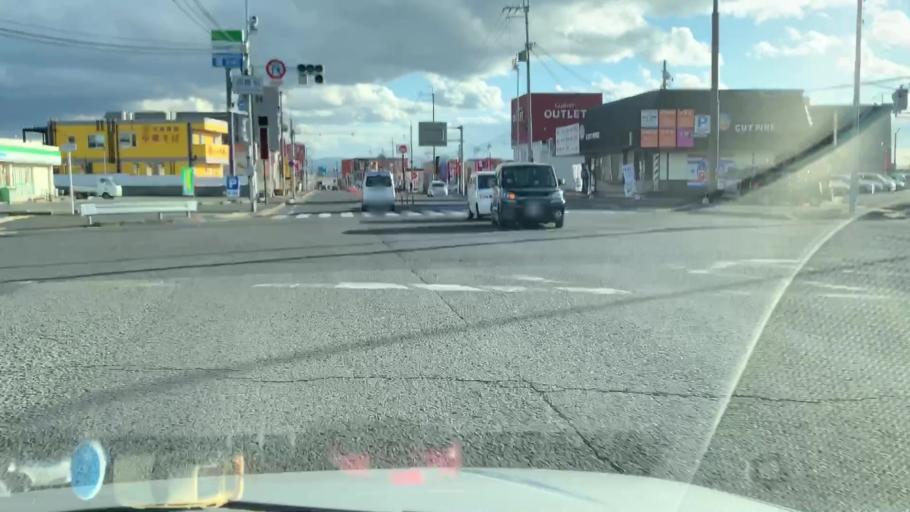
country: JP
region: Wakayama
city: Wakayama-shi
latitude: 34.2373
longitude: 135.1530
